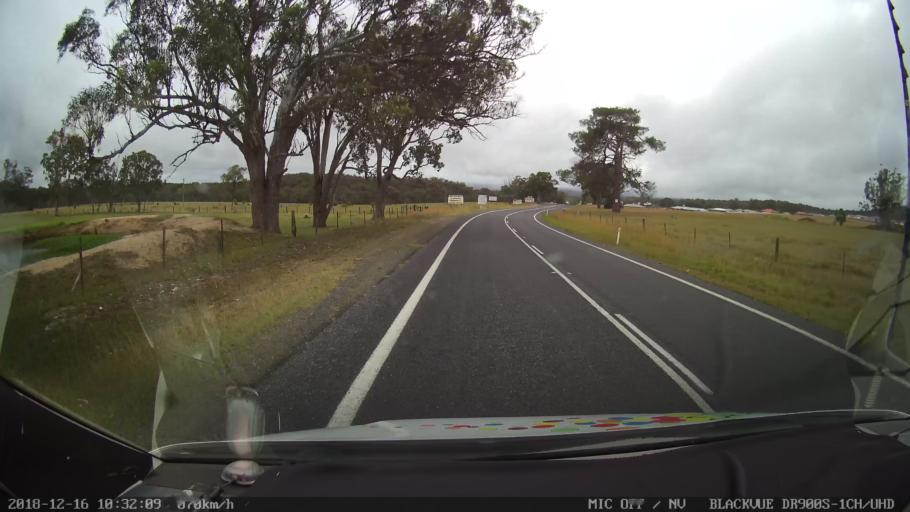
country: AU
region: New South Wales
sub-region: Tenterfield Municipality
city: Carrolls Creek
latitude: -29.0753
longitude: 152.0101
